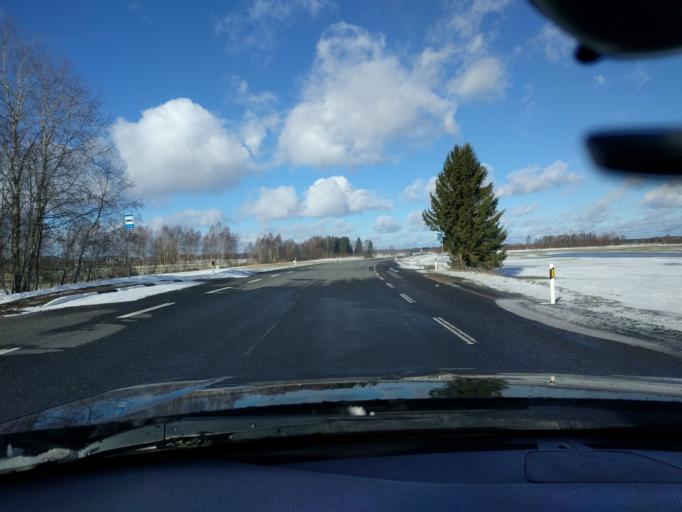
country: EE
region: Harju
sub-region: Anija vald
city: Kehra
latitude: 59.2438
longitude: 25.3556
